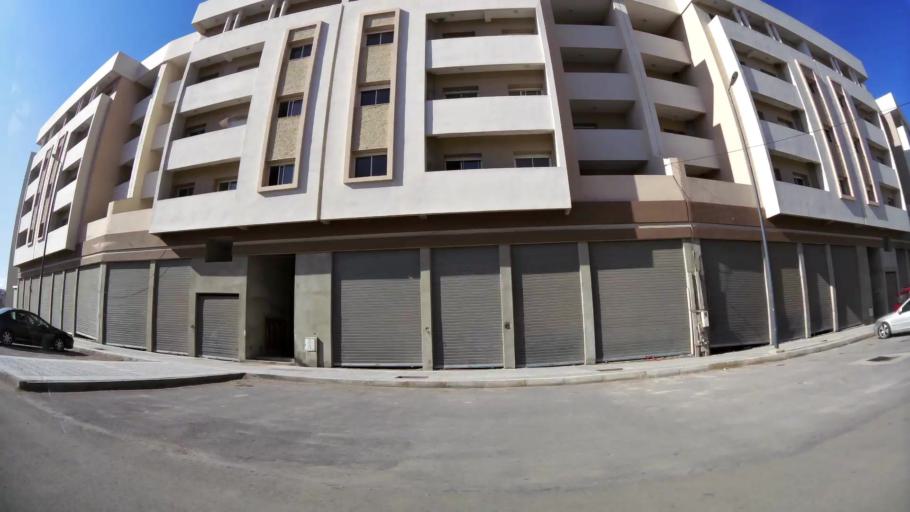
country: MA
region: Oriental
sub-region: Oujda-Angad
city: Oujda
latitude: 34.6792
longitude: -1.9289
